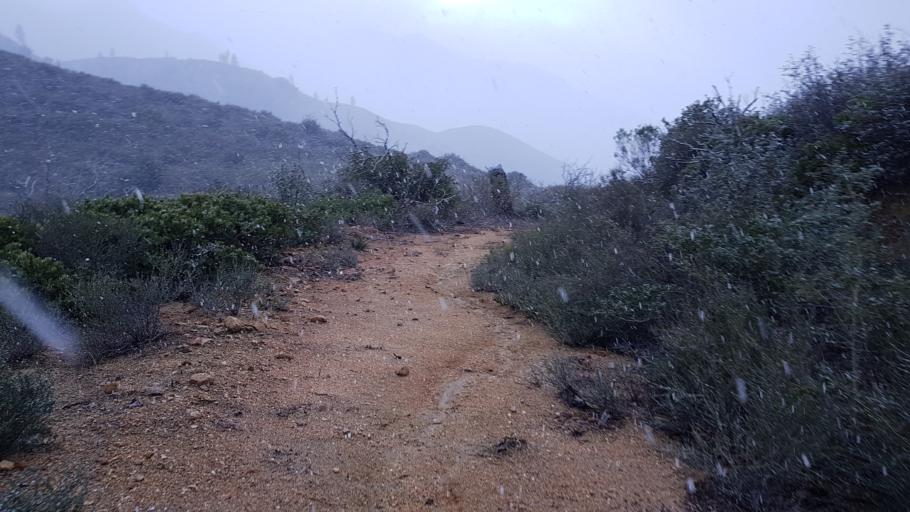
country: US
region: California
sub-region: Riverside County
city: Aguanga
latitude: 33.4009
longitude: -116.9726
